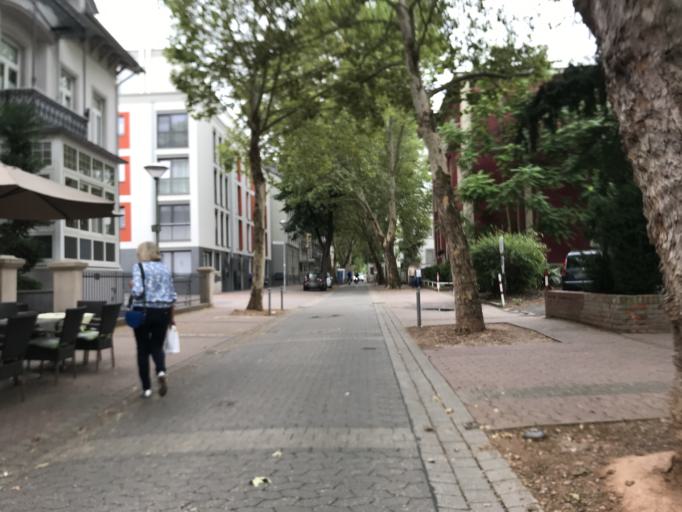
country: DE
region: Rheinland-Pfalz
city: Bad Kreuznach
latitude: 49.8429
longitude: 7.8559
